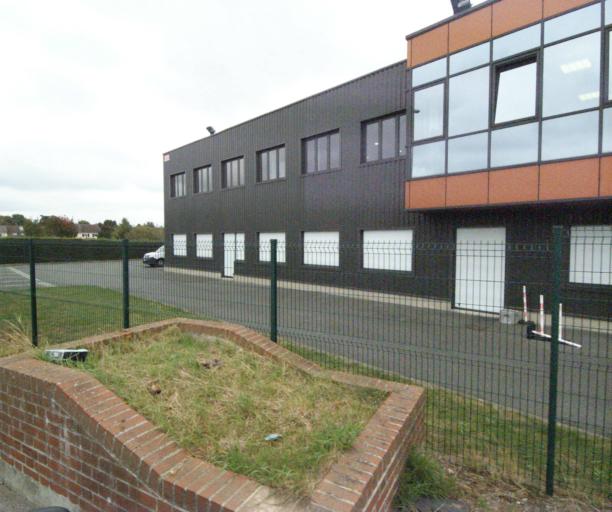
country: FR
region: Nord-Pas-de-Calais
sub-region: Departement du Nord
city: Lezennes
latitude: 50.6114
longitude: 3.1066
